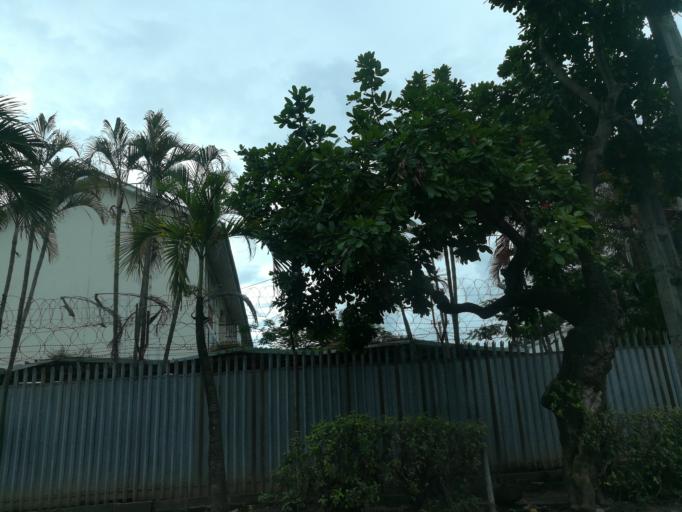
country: NG
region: Lagos
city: Lagos
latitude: 6.4359
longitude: 3.4114
